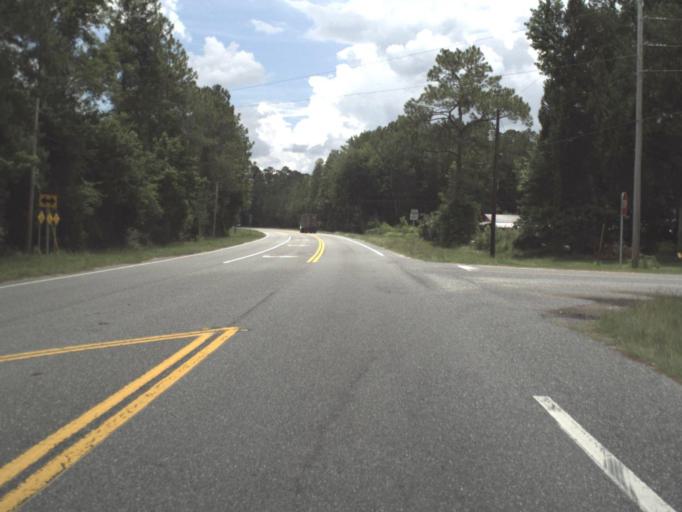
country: US
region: Florida
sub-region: Bradford County
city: Starke
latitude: 29.9457
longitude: -82.1377
